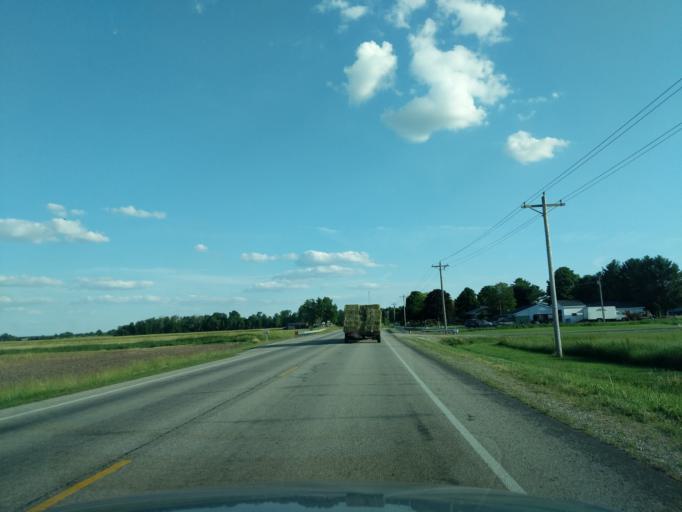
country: US
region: Indiana
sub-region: Huntington County
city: Roanoke
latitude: 41.0160
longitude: -85.4707
